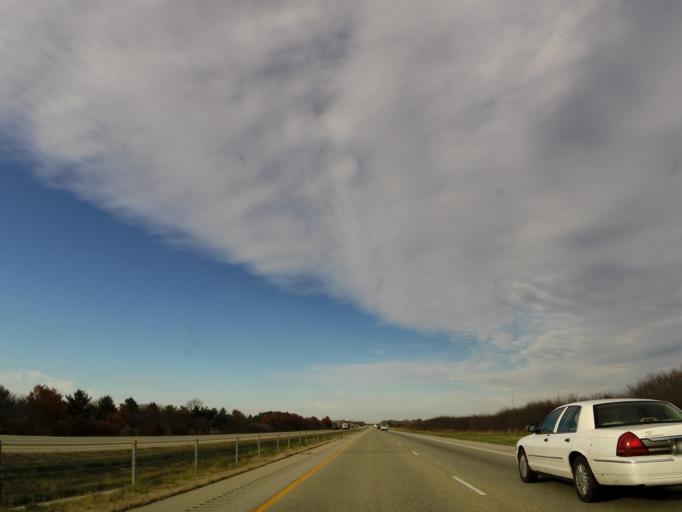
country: US
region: Illinois
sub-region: Champaign County
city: Saint Joseph
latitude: 40.1203
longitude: -88.0260
